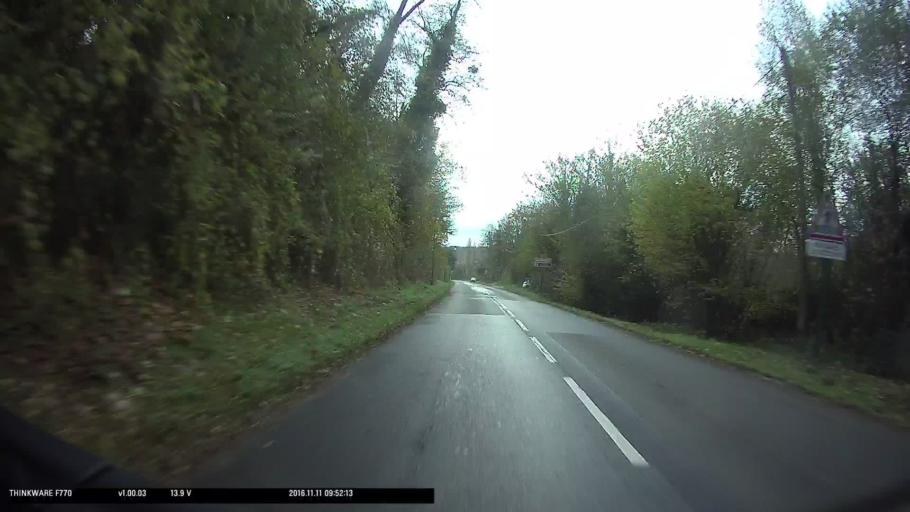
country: FR
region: Ile-de-France
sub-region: Departement du Val-d'Oise
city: Ableiges
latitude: 49.0824
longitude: 2.0009
